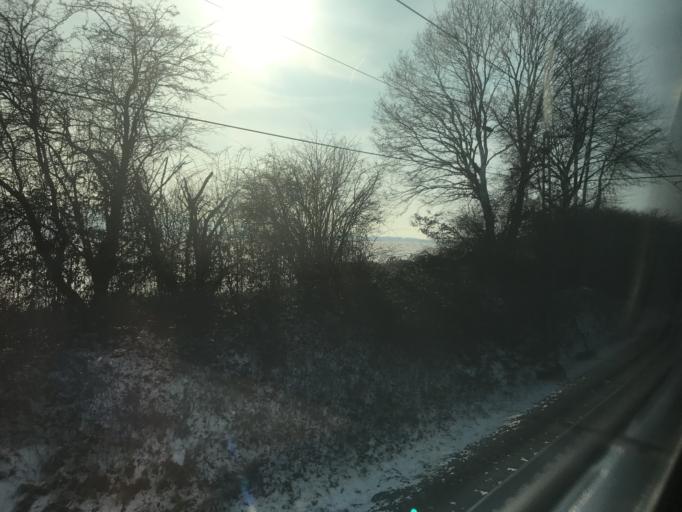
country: DE
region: Rheinland-Pfalz
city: Altrich
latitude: 49.9434
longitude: 6.9012
